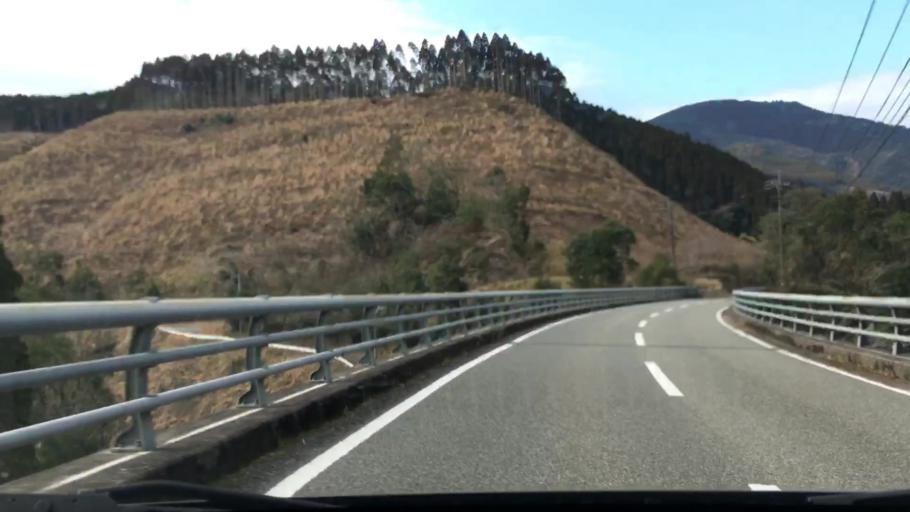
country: JP
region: Miyazaki
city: Nichinan
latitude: 31.7077
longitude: 131.3269
